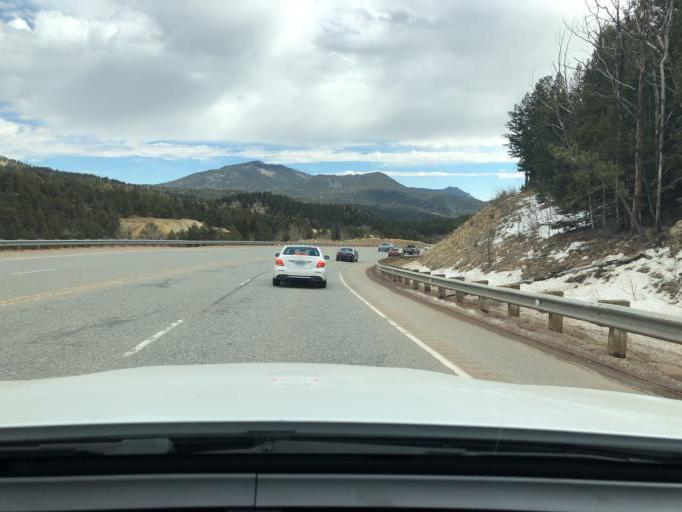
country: US
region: Colorado
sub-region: Gilpin County
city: Central City
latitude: 39.7861
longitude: -105.4886
